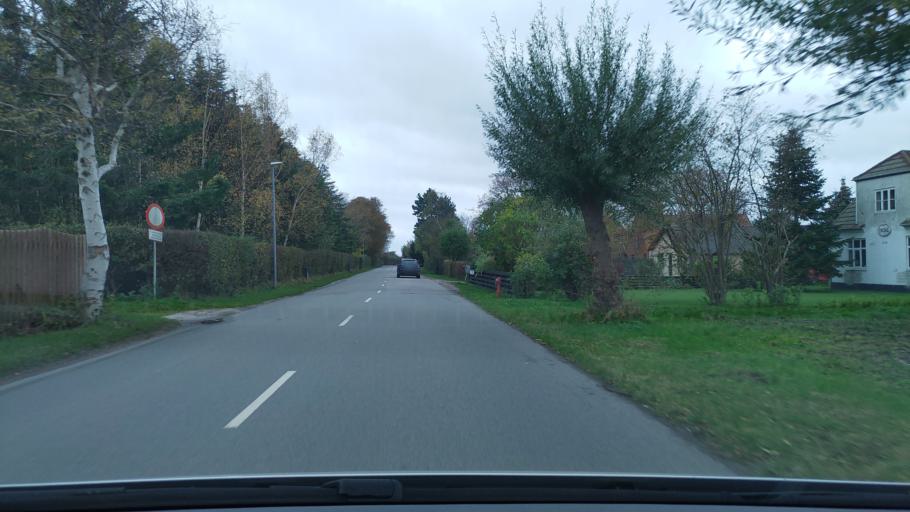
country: DK
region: Capital Region
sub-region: Tarnby Kommune
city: Tarnby
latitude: 55.6011
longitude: 12.6039
